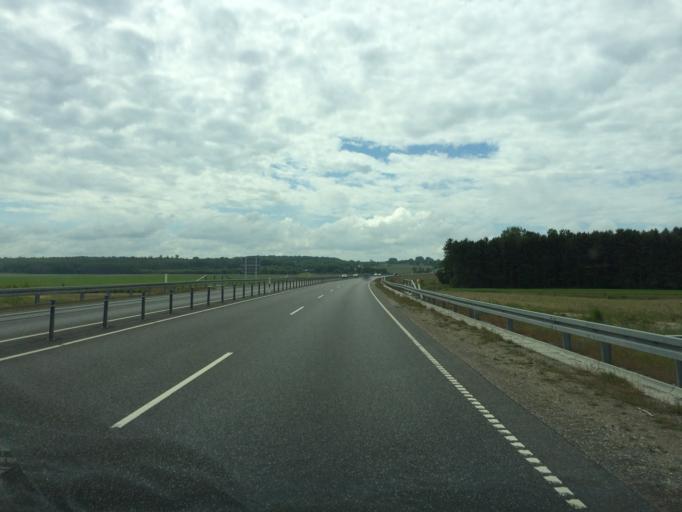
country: DK
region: Zealand
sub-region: Odsherred Kommune
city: Hojby
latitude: 55.8417
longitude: 11.6008
